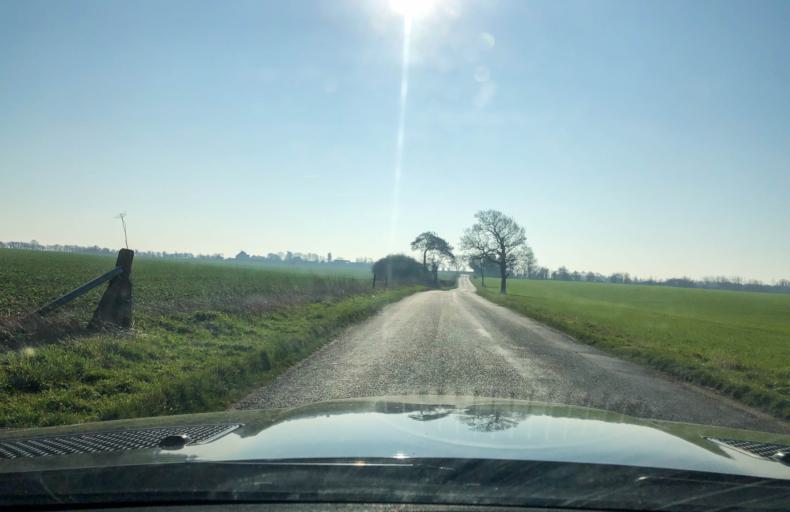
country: GB
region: England
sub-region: Warwickshire
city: Wellesbourne Mountford
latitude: 52.1728
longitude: -1.5252
